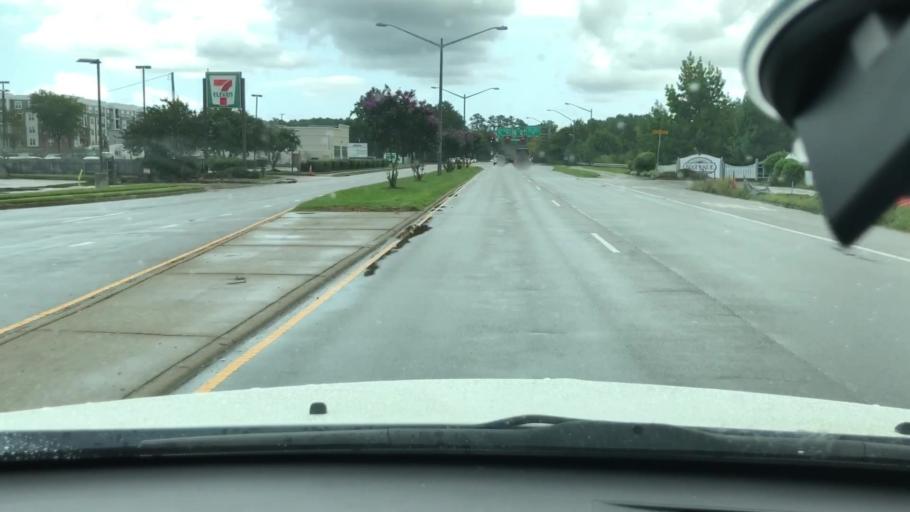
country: US
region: Virginia
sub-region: City of Chesapeake
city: Chesapeake
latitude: 36.8285
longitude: -76.1416
